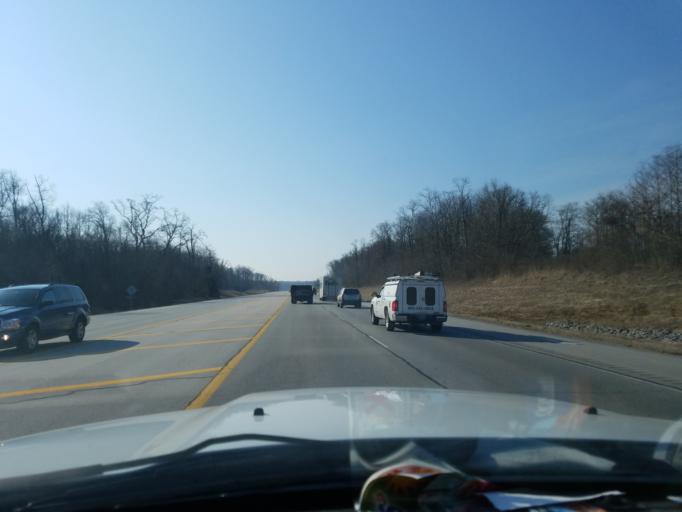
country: US
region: Indiana
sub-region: Monroe County
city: Ellettsville
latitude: 39.2064
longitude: -86.5793
